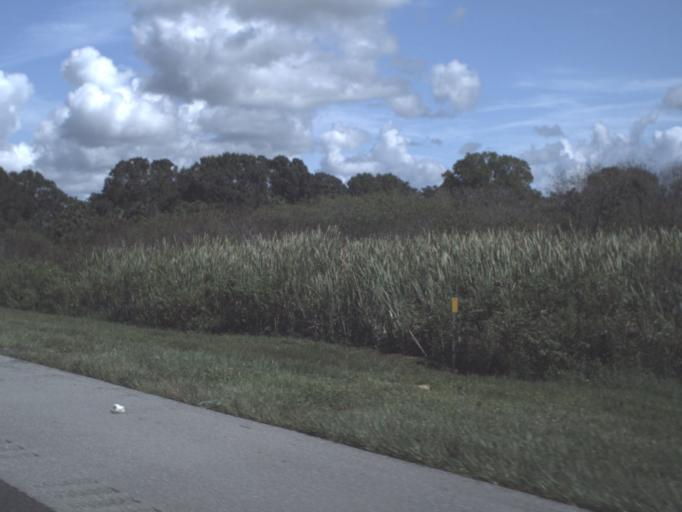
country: US
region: Florida
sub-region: Sarasota County
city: Laurel
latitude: 27.1757
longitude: -82.4346
